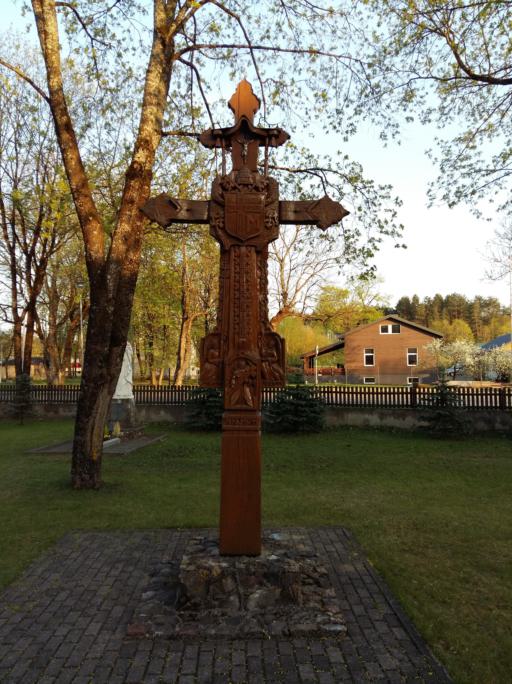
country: LT
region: Alytaus apskritis
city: Varena
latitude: 54.2101
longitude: 24.5718
